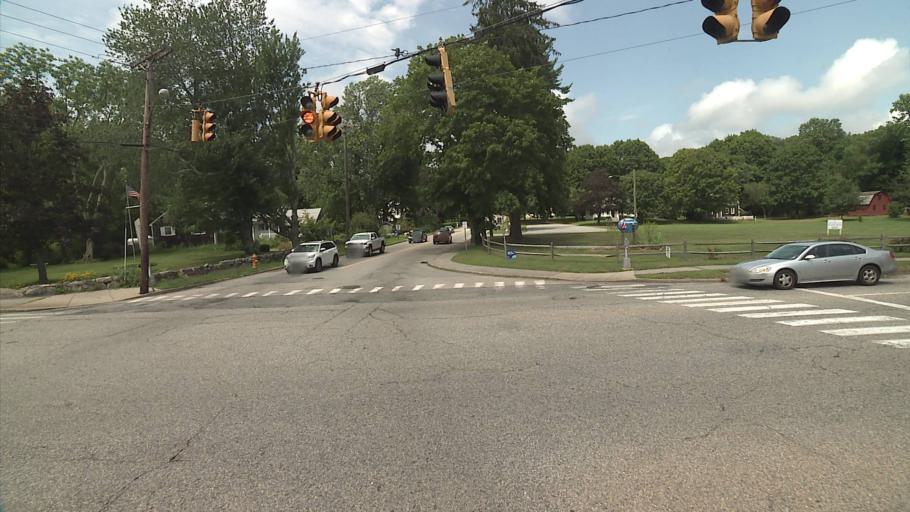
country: US
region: Connecticut
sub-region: New London County
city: Central Waterford
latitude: 41.3408
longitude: -72.1384
